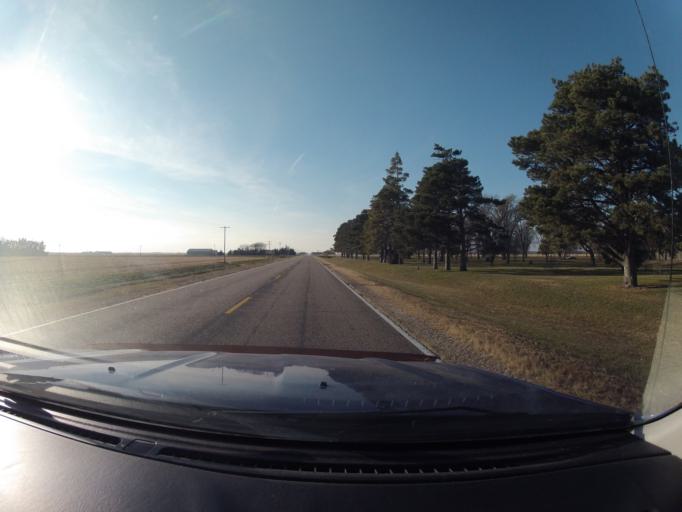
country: US
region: Nebraska
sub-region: Buffalo County
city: Kearney
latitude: 40.6410
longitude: -99.0056
